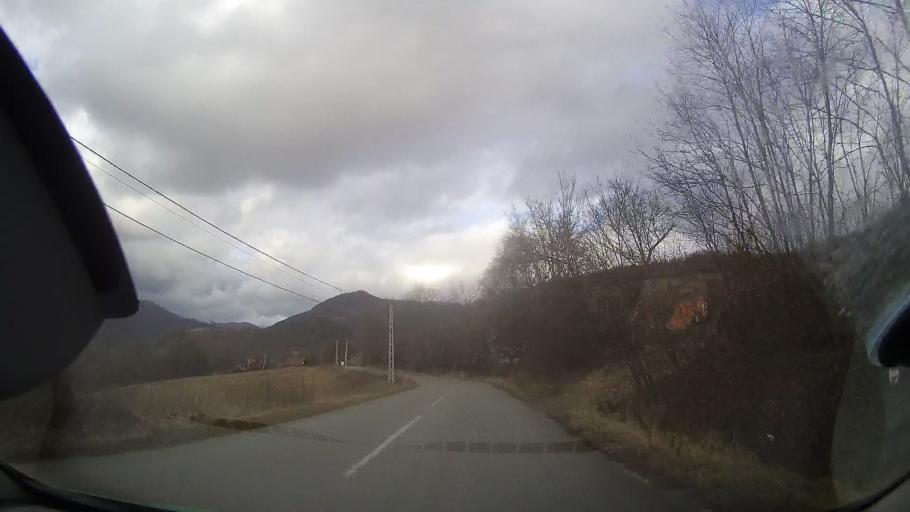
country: RO
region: Alba
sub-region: Comuna Rimetea
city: Rimetea
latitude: 46.4722
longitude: 23.5841
